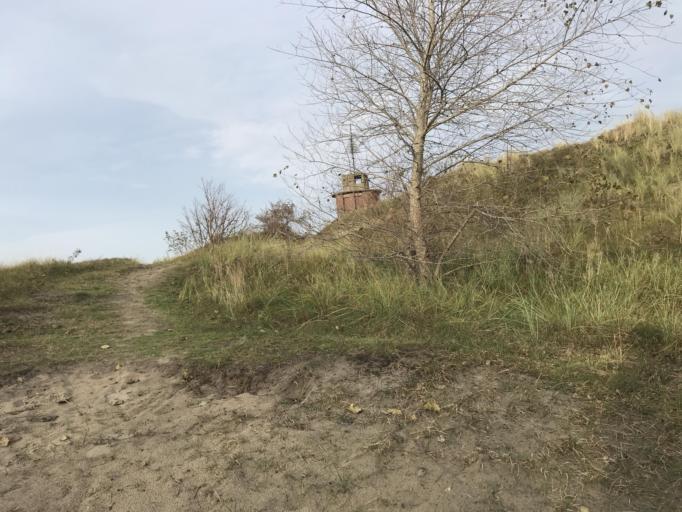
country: DE
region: Lower Saxony
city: Borkum
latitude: 53.6059
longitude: 6.7624
